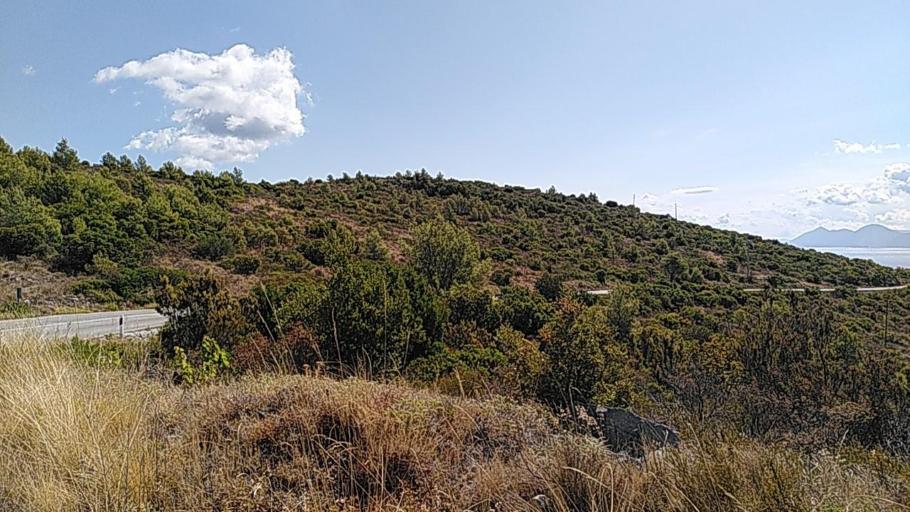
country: HR
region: Splitsko-Dalmatinska
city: Tucepi
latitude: 43.1271
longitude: 17.0963
